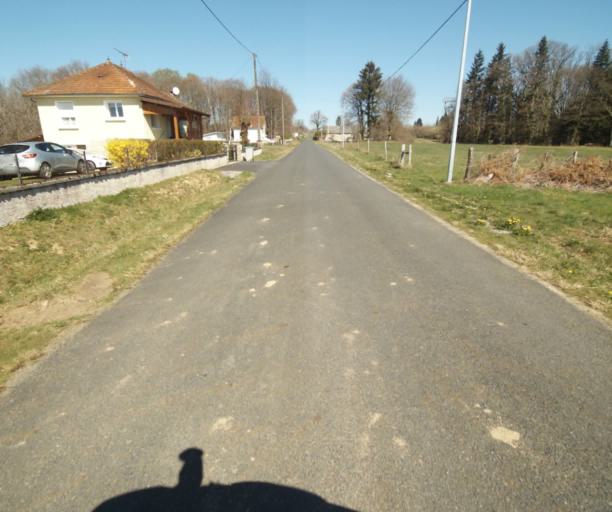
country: FR
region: Limousin
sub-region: Departement de la Correze
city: Saint-Mexant
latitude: 45.3171
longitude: 1.6465
